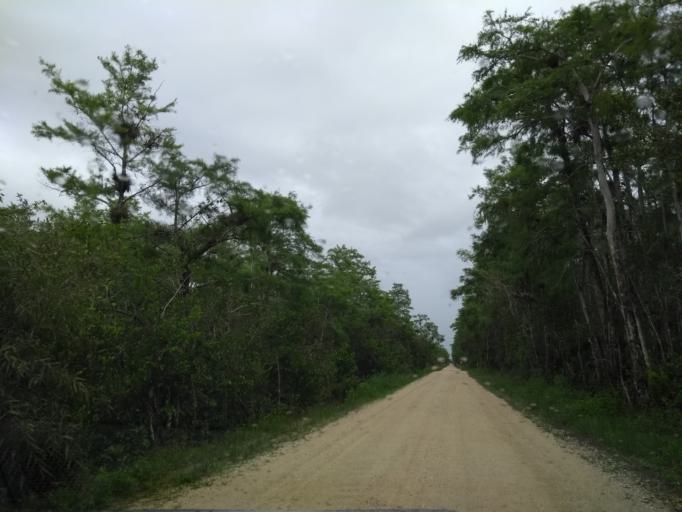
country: US
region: Florida
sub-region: Miami-Dade County
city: The Hammocks
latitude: 25.7503
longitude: -80.9655
